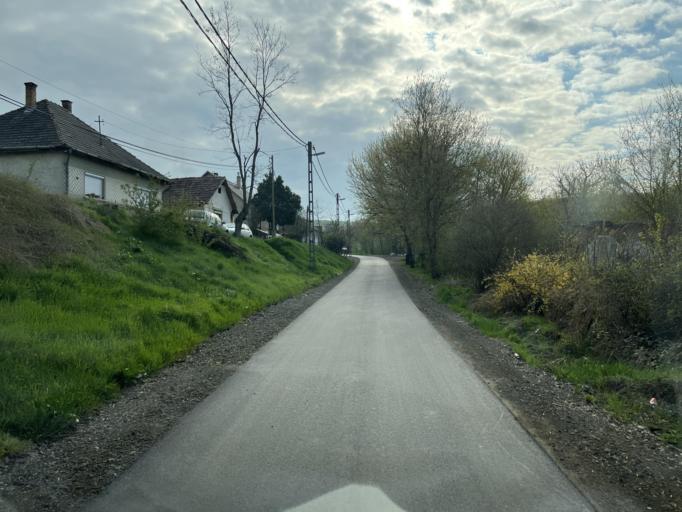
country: HU
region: Pest
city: Galgamacsa
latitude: 47.7424
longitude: 19.3807
